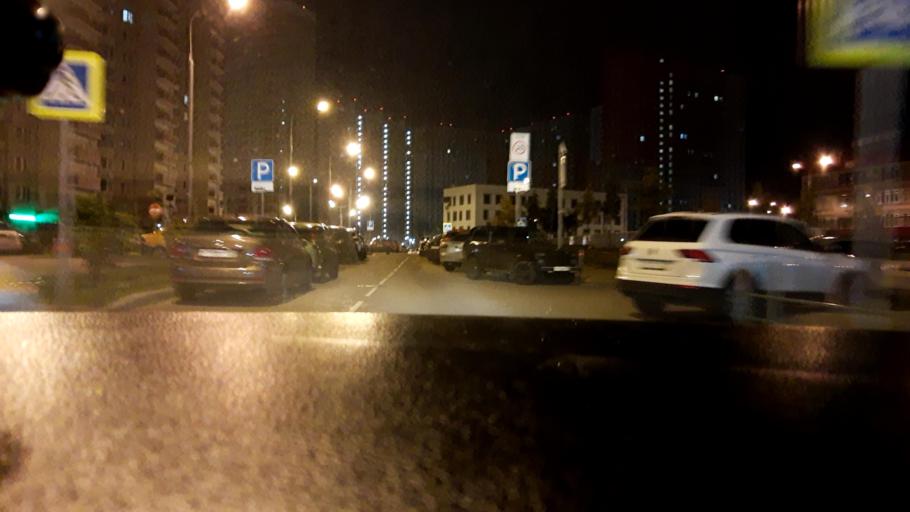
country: RU
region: Moscow
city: Khimki
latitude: 55.8737
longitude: 37.3988
